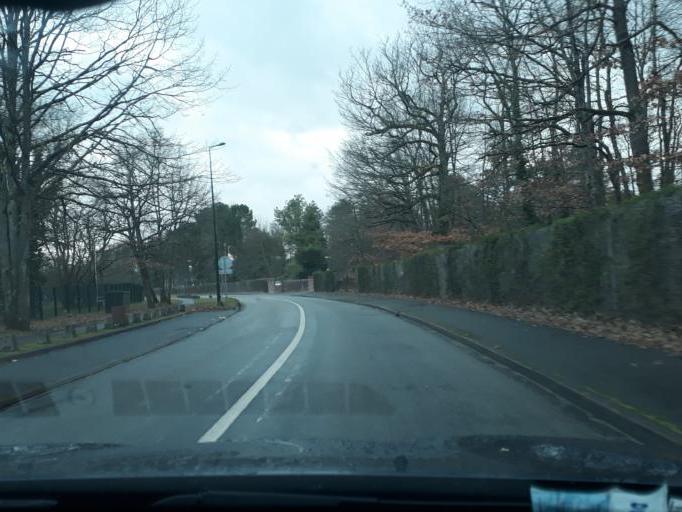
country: FR
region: Centre
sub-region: Departement du Loiret
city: Olivet
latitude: 47.8290
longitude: 1.9151
